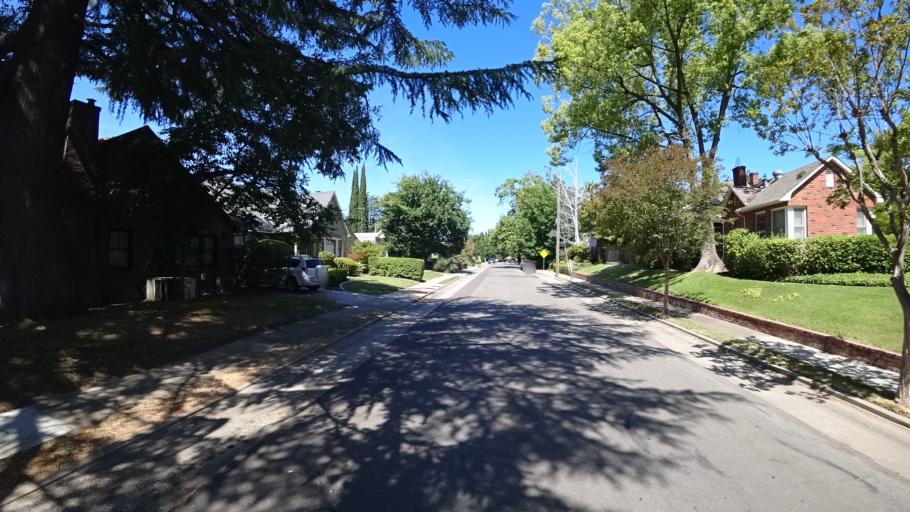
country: US
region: California
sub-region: Sacramento County
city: Sacramento
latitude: 38.5573
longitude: -121.5035
